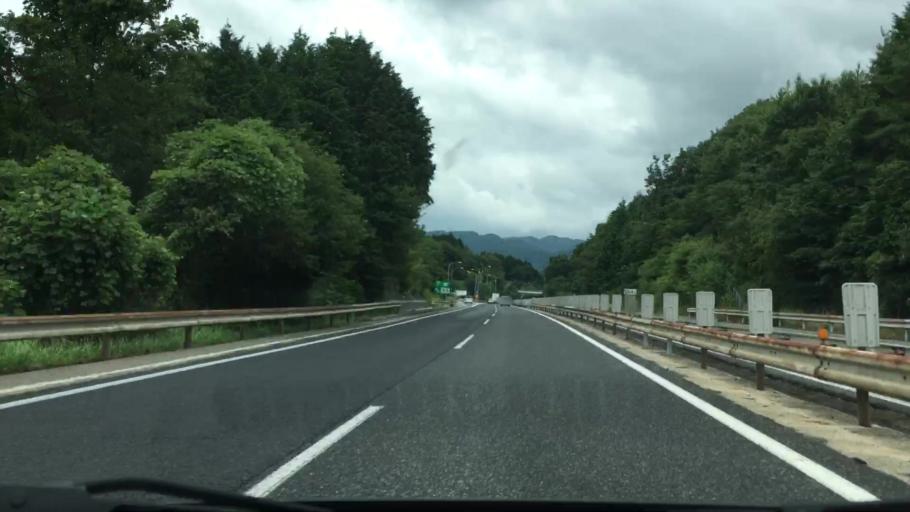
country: JP
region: Okayama
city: Takahashi
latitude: 35.0129
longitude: 133.7297
